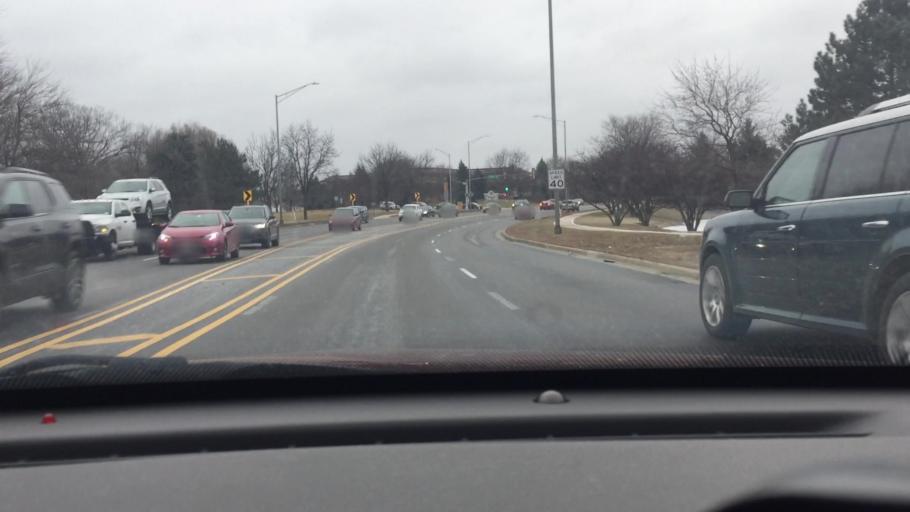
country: US
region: Illinois
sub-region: DuPage County
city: Warrenville
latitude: 41.7861
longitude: -88.1835
